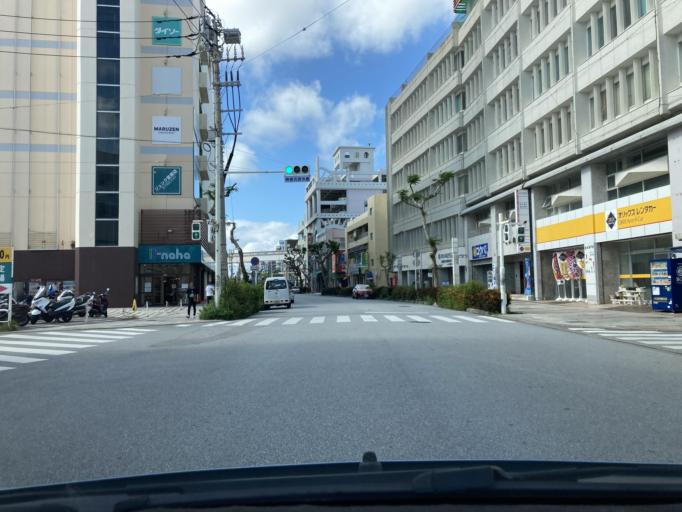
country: JP
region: Okinawa
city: Naha-shi
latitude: 26.2185
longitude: 127.6865
